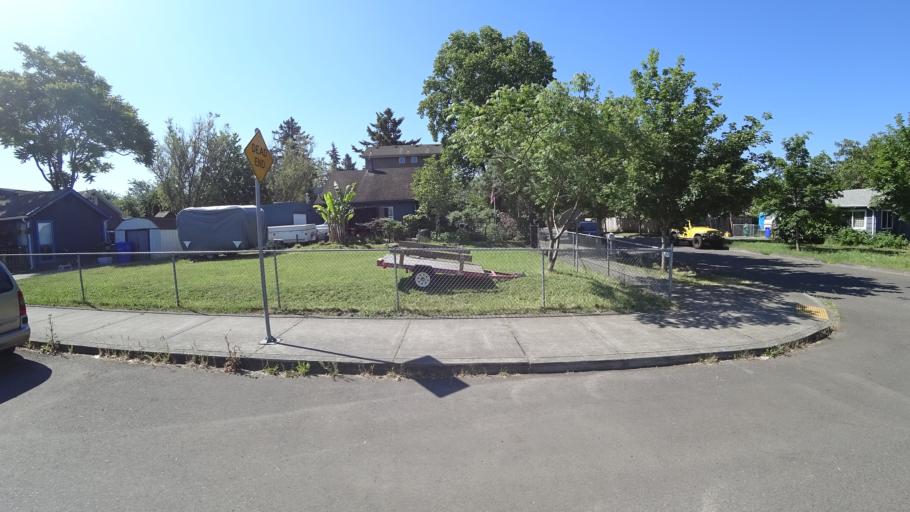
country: US
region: Oregon
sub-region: Multnomah County
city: Lents
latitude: 45.4811
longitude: -122.5557
